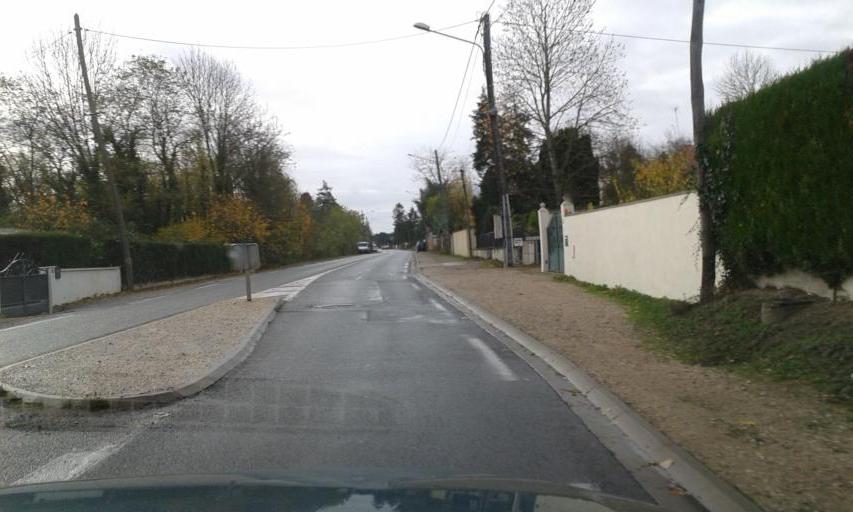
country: FR
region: Centre
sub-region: Departement du Loiret
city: Saint-Ay
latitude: 47.8528
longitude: 1.7407
